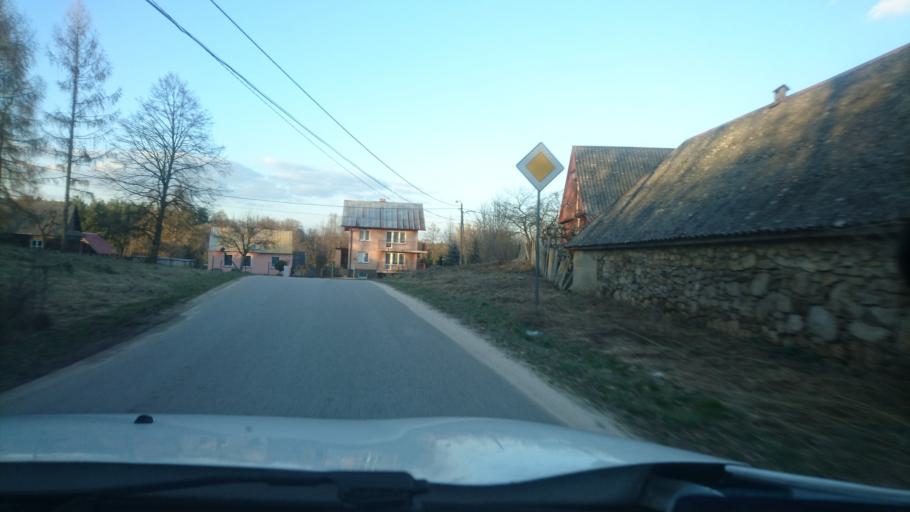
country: PL
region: Swietokrzyskie
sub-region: Powiat kielecki
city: Morawica
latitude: 50.7783
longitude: 20.7052
